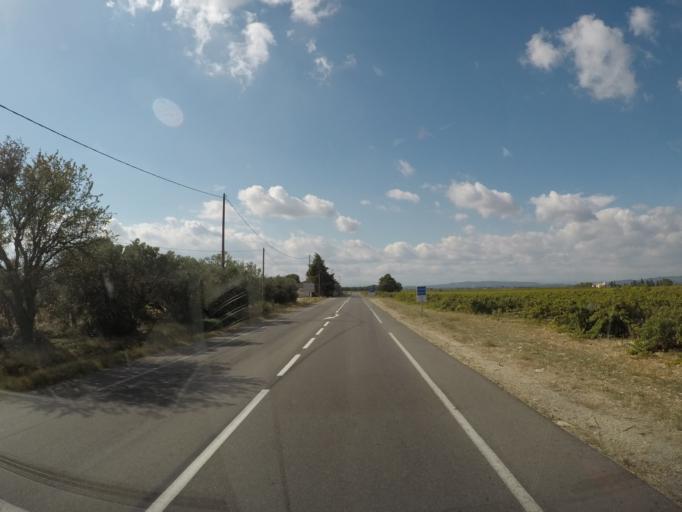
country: FR
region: Rhone-Alpes
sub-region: Departement de la Drome
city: Tulette
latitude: 44.2767
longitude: 4.9155
